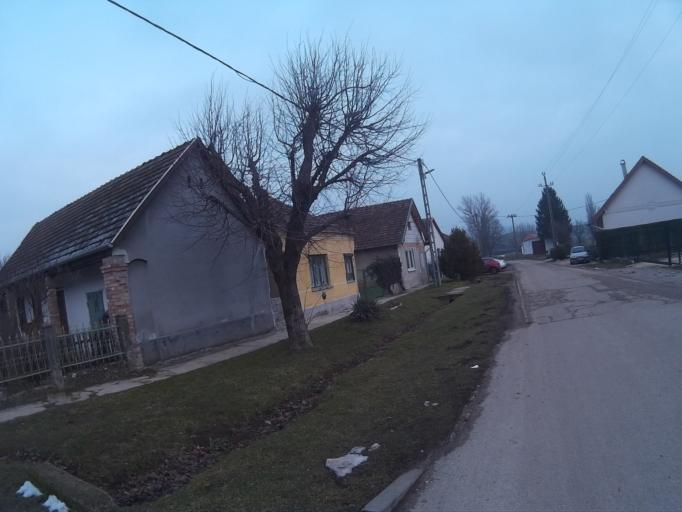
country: HU
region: Komarom-Esztergom
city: Tarjan
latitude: 47.6440
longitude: 18.5157
